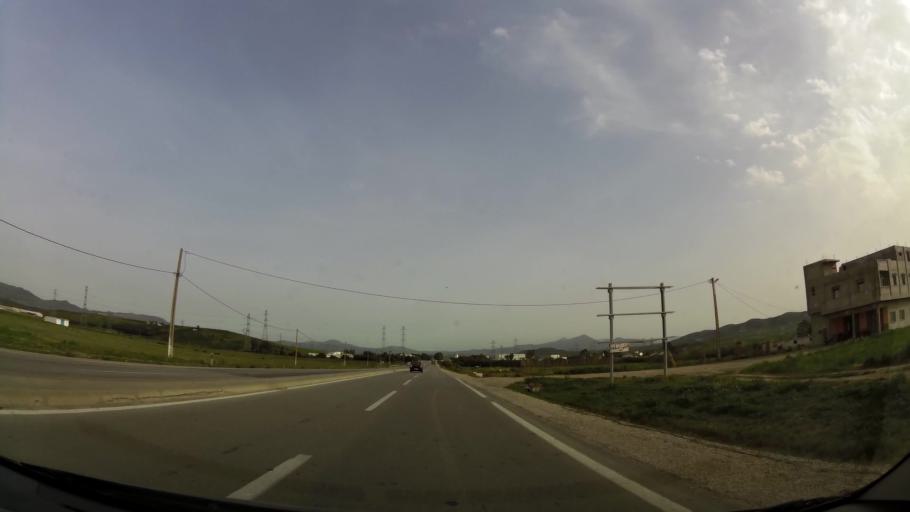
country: MA
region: Tanger-Tetouan
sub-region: Tanger-Assilah
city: Dar Chaoui
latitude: 35.6174
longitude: -5.6670
